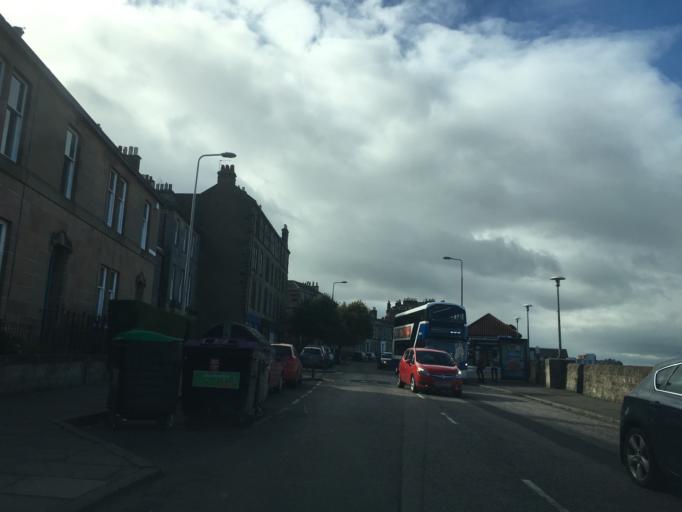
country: GB
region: Scotland
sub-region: Edinburgh
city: Edinburgh
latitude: 55.9799
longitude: -3.2028
